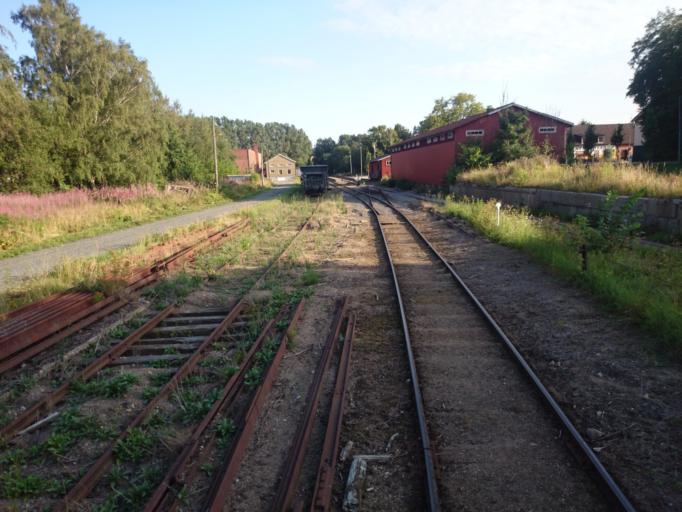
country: SE
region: Skane
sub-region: Simrishamns Kommun
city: Kivik
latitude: 55.6860
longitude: 14.1552
